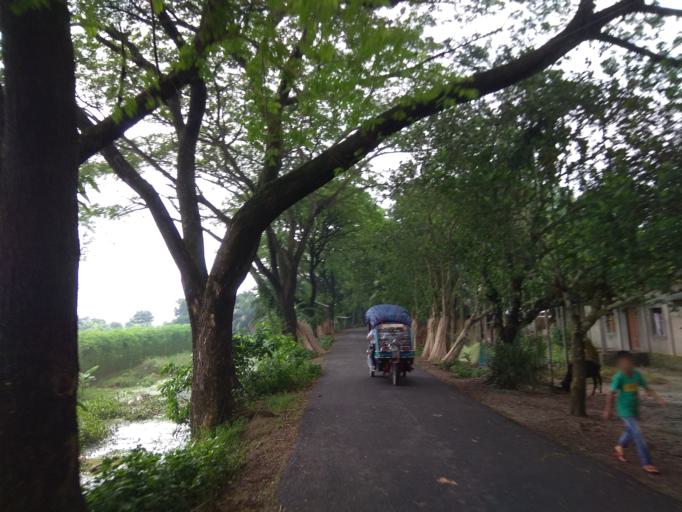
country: BD
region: Dhaka
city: Dohar
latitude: 23.4756
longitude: 90.0541
